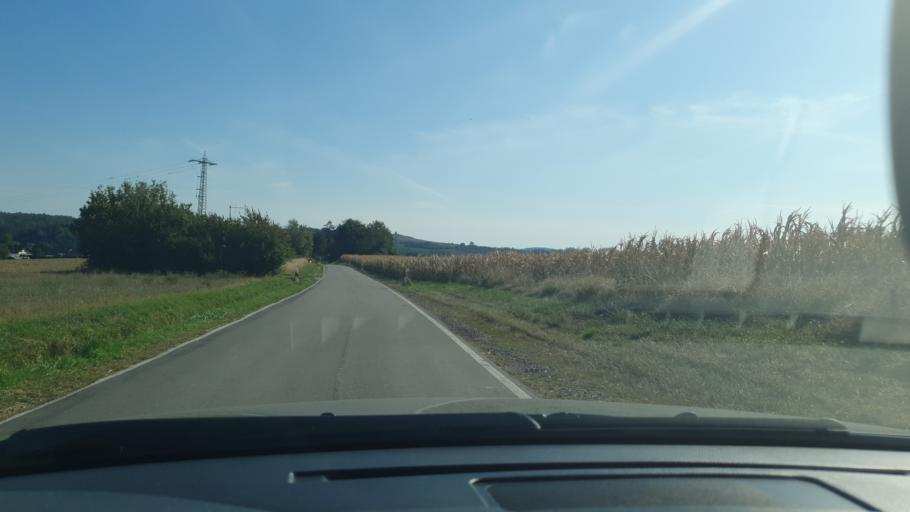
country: DE
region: Rheinland-Pfalz
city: Battweiler
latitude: 49.2842
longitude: 7.4642
